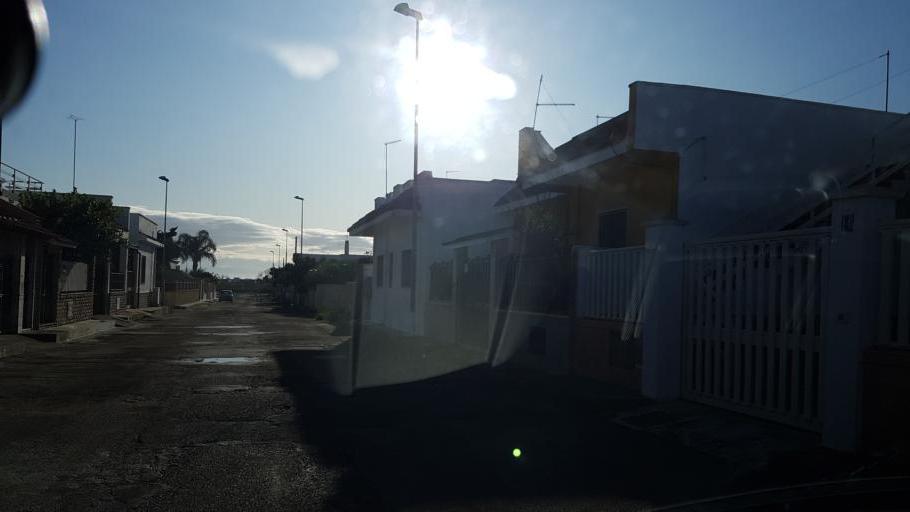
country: IT
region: Apulia
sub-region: Provincia di Brindisi
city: Torchiarolo
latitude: 40.5349
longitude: 18.0705
